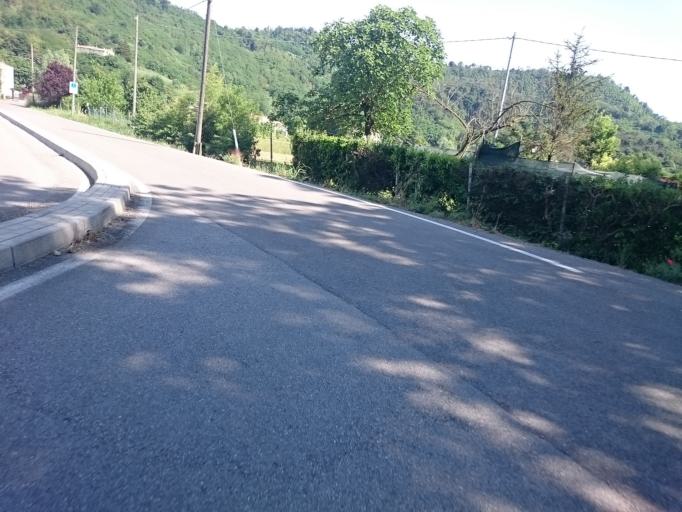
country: IT
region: Veneto
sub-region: Provincia di Padova
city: Treponti
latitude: 45.3672
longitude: 11.7187
